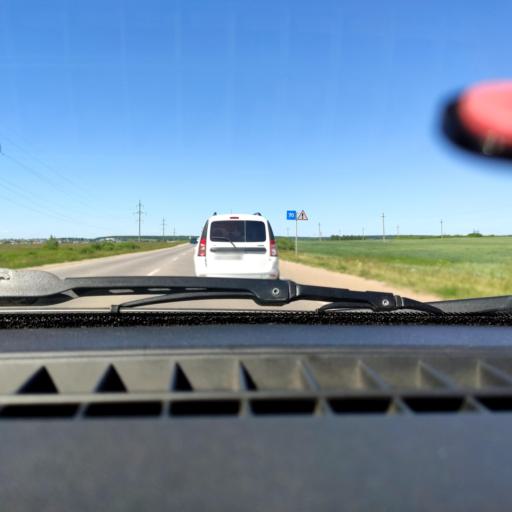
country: RU
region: Bashkortostan
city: Iglino
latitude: 54.8903
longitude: 56.4718
